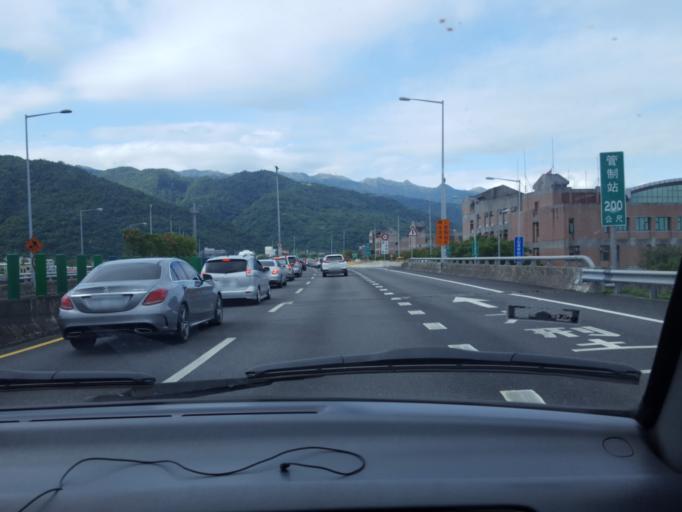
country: TW
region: Taiwan
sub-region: Yilan
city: Yilan
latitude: 24.8316
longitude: 121.7909
